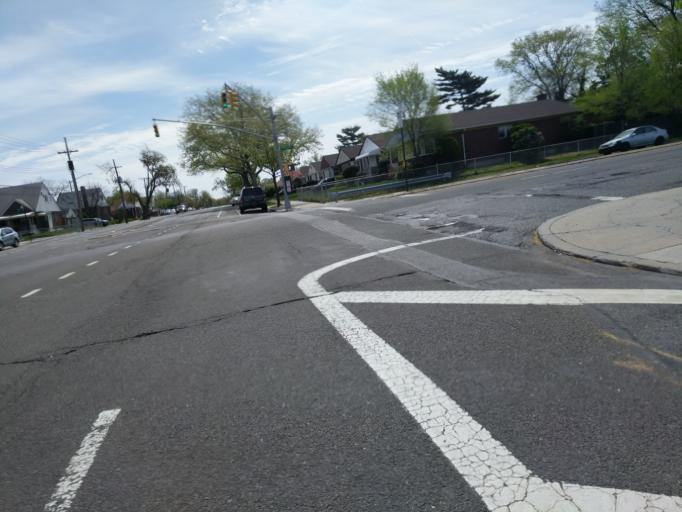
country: US
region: New York
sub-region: Nassau County
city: Elmont
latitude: 40.6855
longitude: -73.7338
